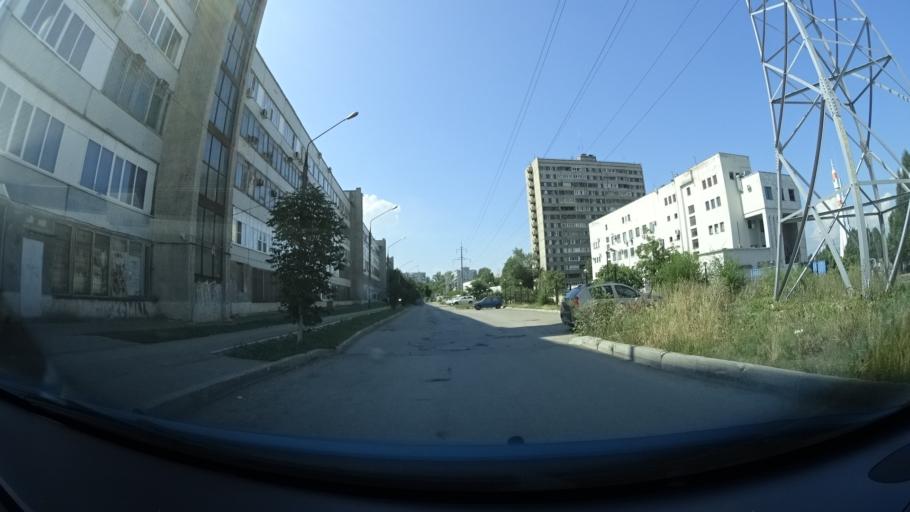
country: RU
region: Samara
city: Samara
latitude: 53.2118
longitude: 50.1485
